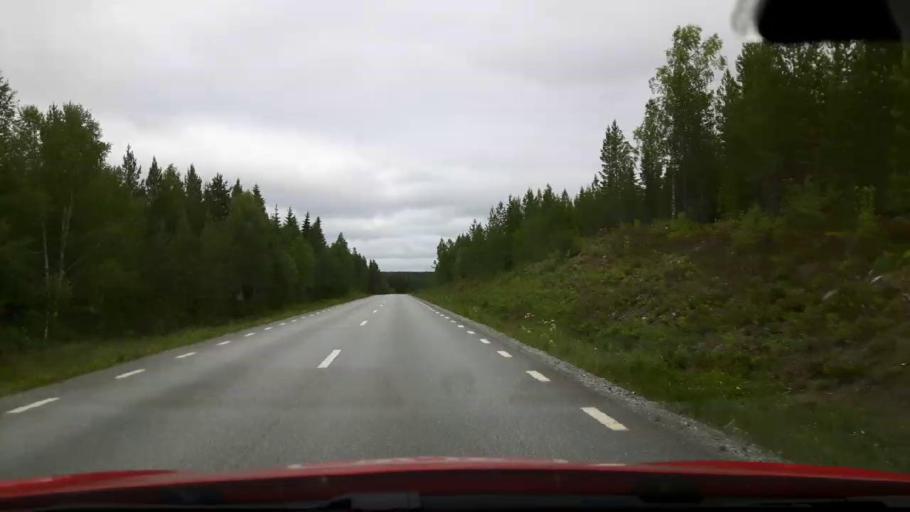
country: SE
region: Jaemtland
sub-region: OEstersunds Kommun
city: Lit
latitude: 63.7260
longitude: 14.7208
